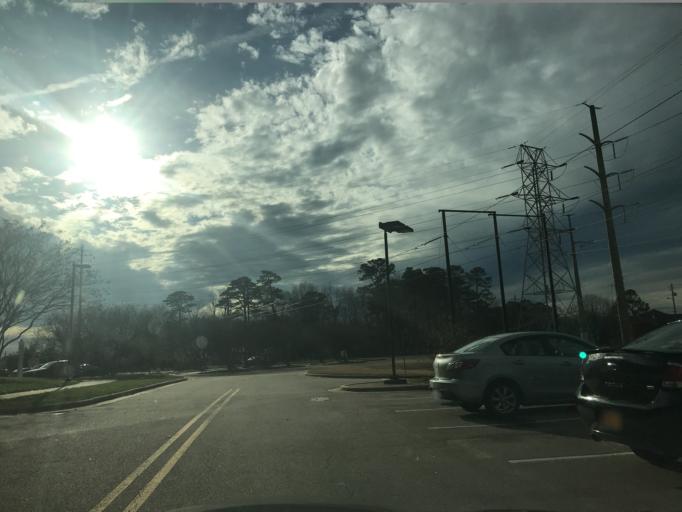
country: US
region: North Carolina
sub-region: Wake County
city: West Raleigh
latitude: 35.7873
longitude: -78.6859
